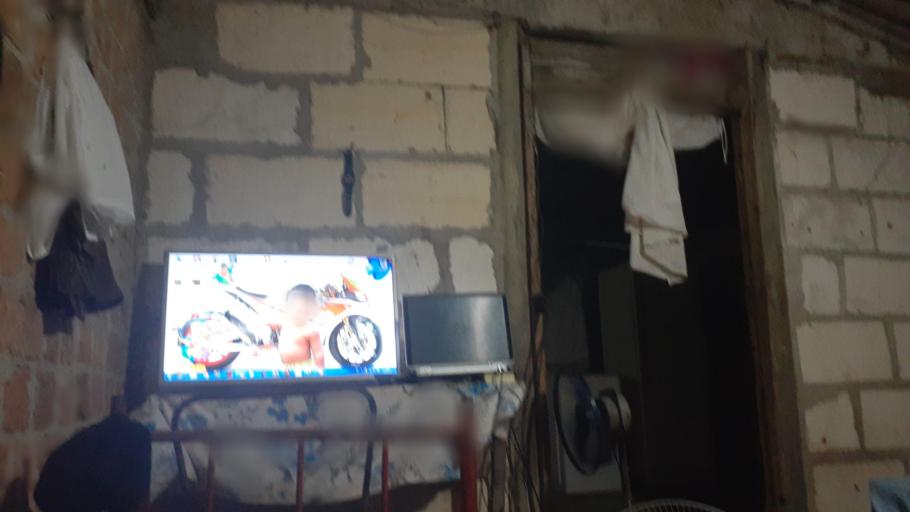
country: CU
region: La Habana
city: Alamar
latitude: 23.1531
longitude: -82.1515
